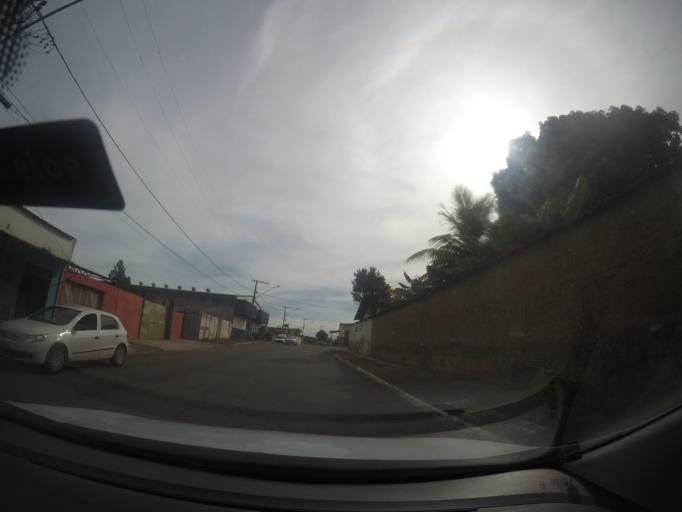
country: BR
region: Goias
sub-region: Goiania
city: Goiania
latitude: -16.6573
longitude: -49.3049
